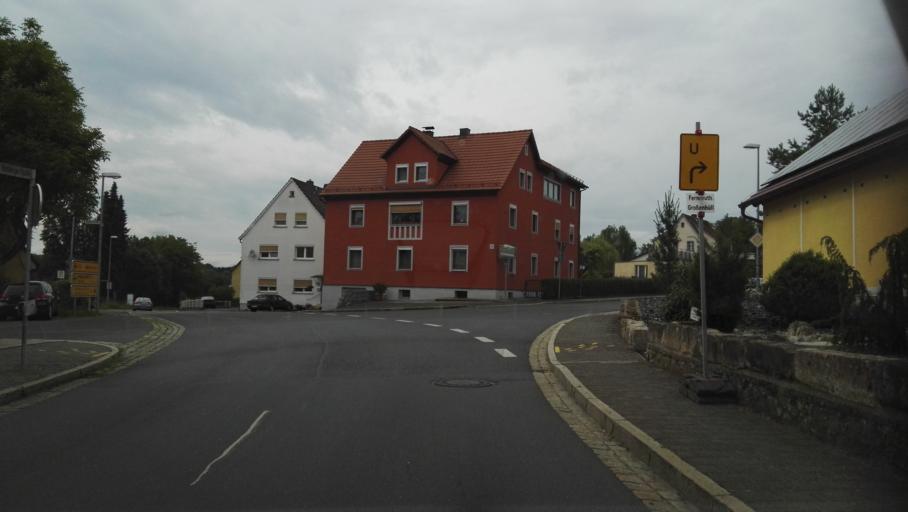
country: DE
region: Bavaria
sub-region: Upper Franconia
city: Hollfeld
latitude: 49.9384
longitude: 11.2888
